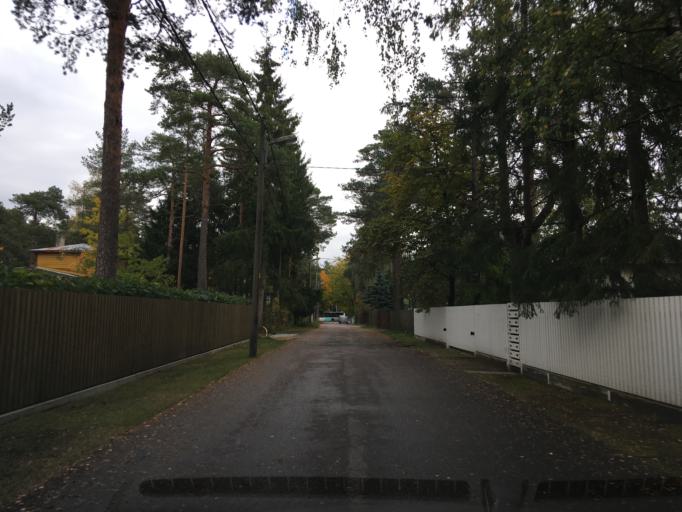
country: EE
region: Harju
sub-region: Tallinna linn
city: Tallinn
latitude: 59.3802
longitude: 24.7148
